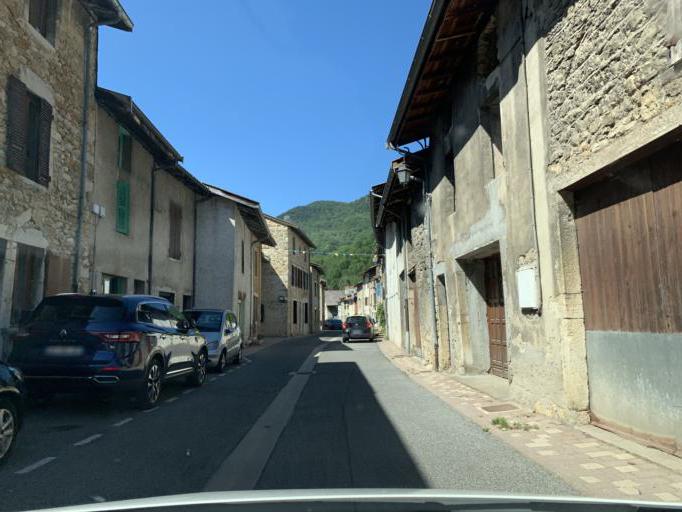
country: FR
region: Rhone-Alpes
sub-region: Departement de l'Ain
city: Vaux-en-Bugey
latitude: 45.9214
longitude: 5.3967
